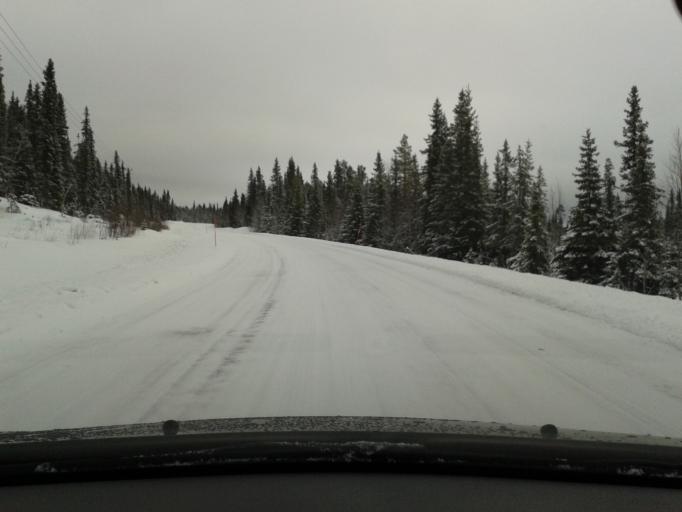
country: SE
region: Vaesterbotten
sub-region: Vilhelmina Kommun
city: Sjoberg
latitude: 65.2350
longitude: 15.8389
